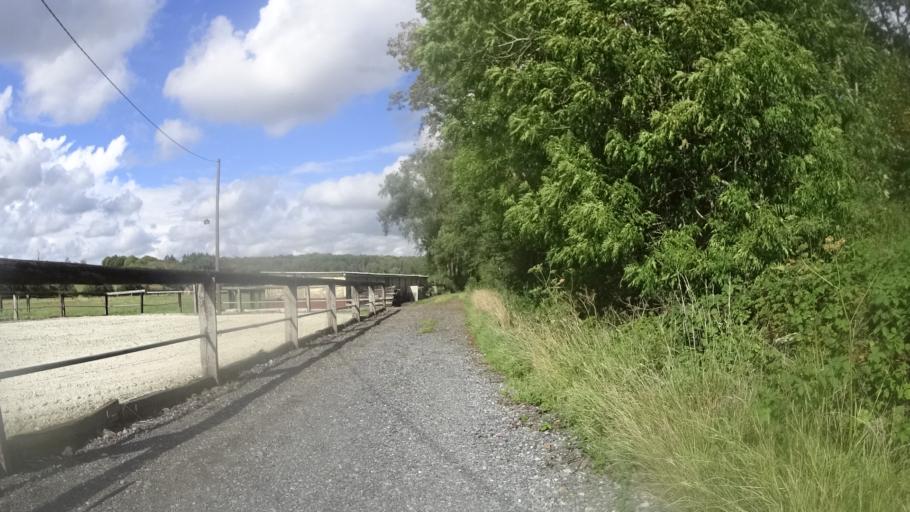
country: BE
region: Wallonia
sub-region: Province du Hainaut
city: Merbes-le-Chateau
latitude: 50.3224
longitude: 4.2111
